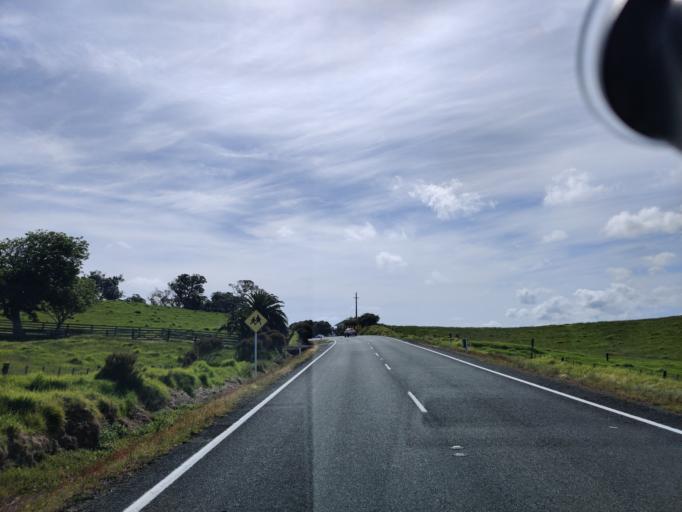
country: NZ
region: Northland
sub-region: Far North District
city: Ahipara
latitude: -35.4986
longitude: 173.4055
